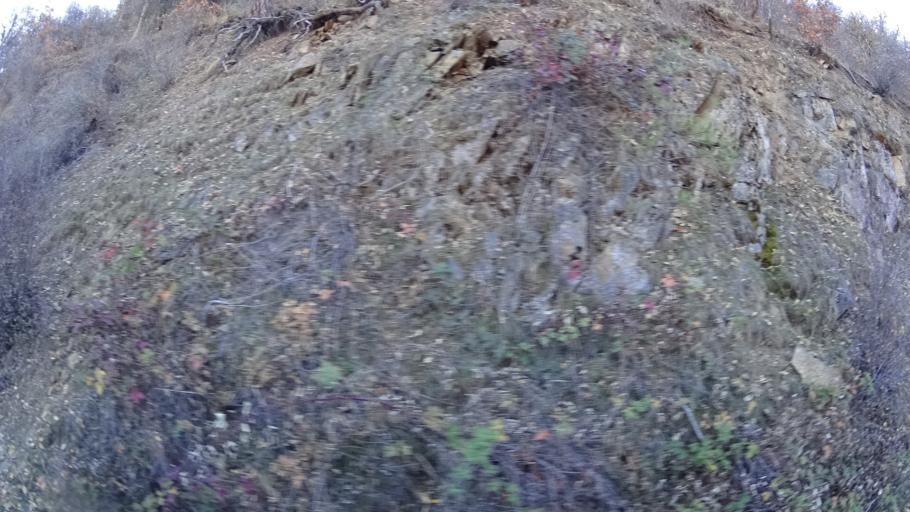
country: US
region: California
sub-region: Siskiyou County
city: Yreka
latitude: 41.8608
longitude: -122.7188
